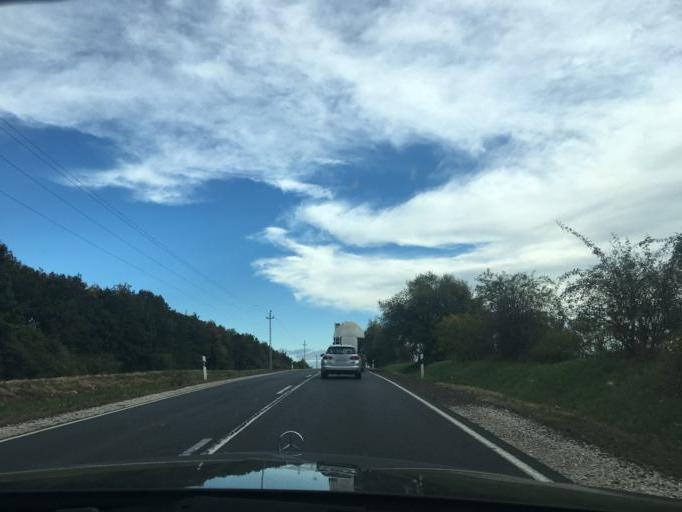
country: HU
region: Borsod-Abauj-Zemplen
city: Arnot
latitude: 48.1266
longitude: 20.8723
